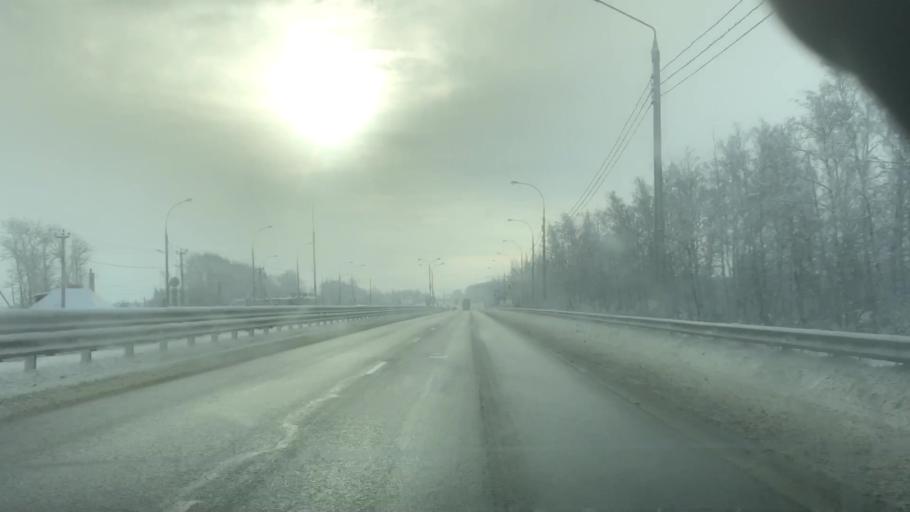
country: RU
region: Tula
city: Venev
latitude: 54.3451
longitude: 38.1546
